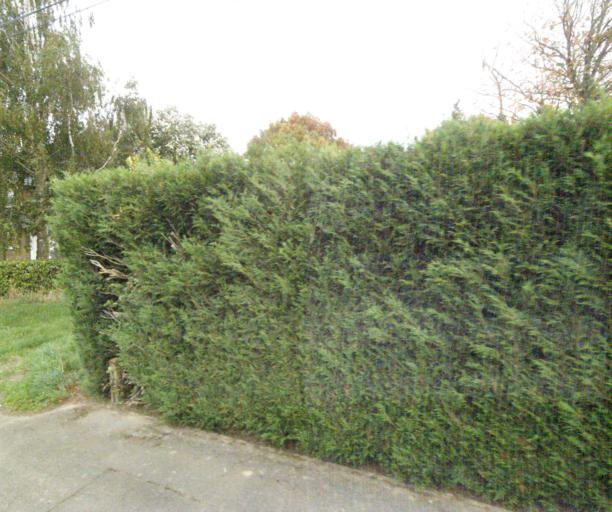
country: FR
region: Nord-Pas-de-Calais
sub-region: Departement du Nord
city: Houplines
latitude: 50.6625
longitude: 2.9102
